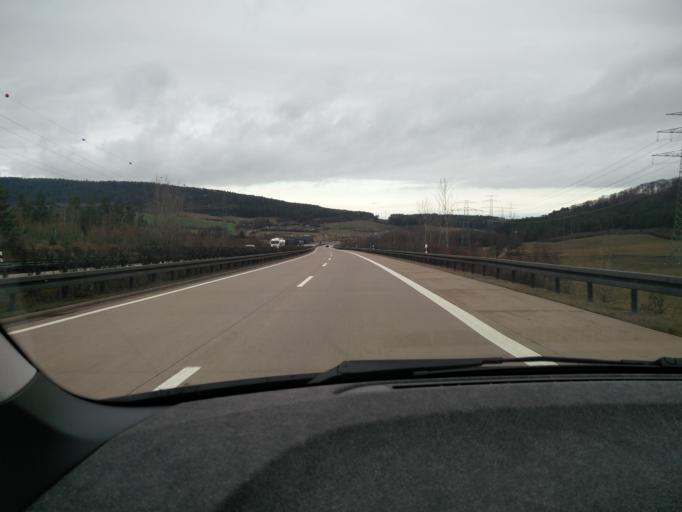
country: DE
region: Thuringia
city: Behringen
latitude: 50.7594
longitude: 11.0049
